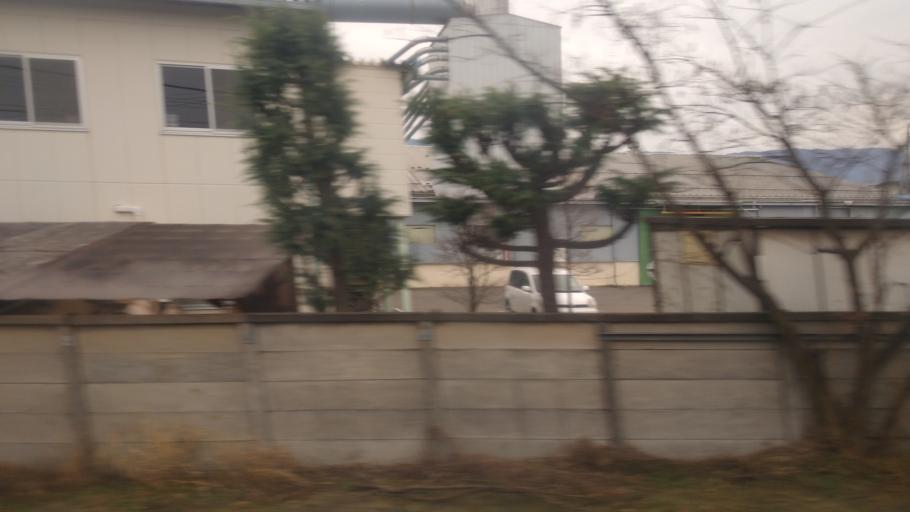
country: JP
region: Nagano
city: Matsumoto
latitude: 36.1881
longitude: 137.9613
